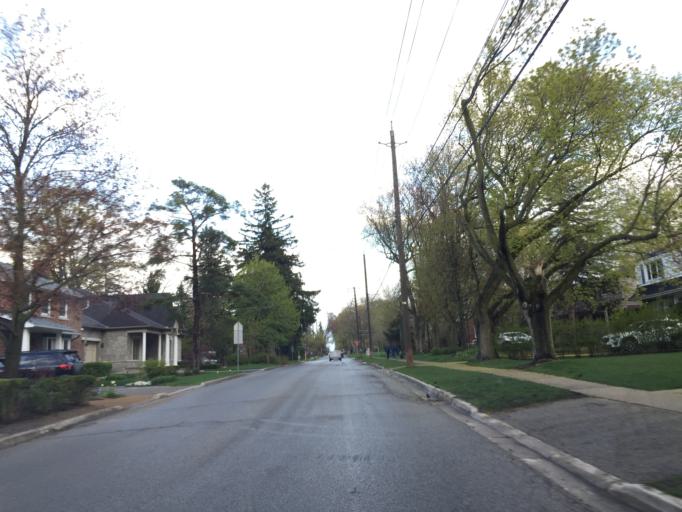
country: CA
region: Ontario
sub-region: Wellington County
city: Guelph
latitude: 43.5537
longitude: -80.2449
